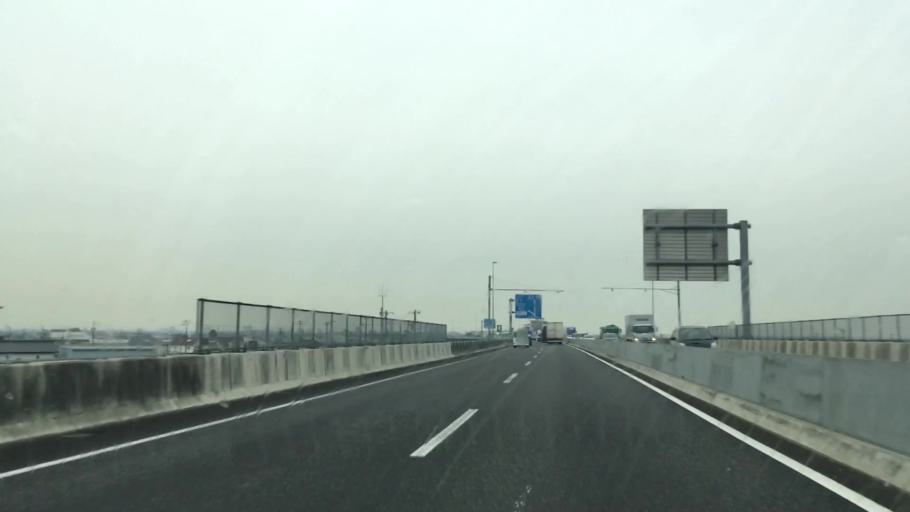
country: JP
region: Aichi
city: Anjo
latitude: 34.9537
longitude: 137.0372
